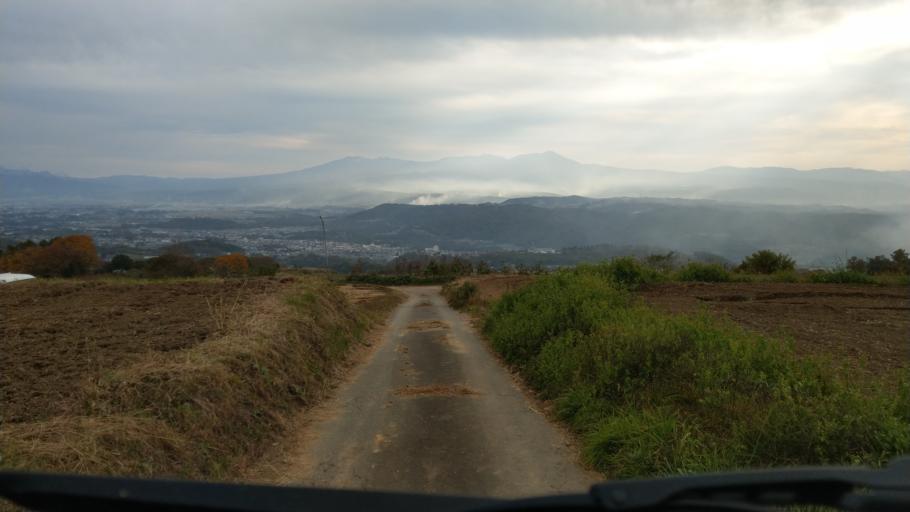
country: JP
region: Nagano
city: Komoro
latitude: 36.3606
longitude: 138.4290
